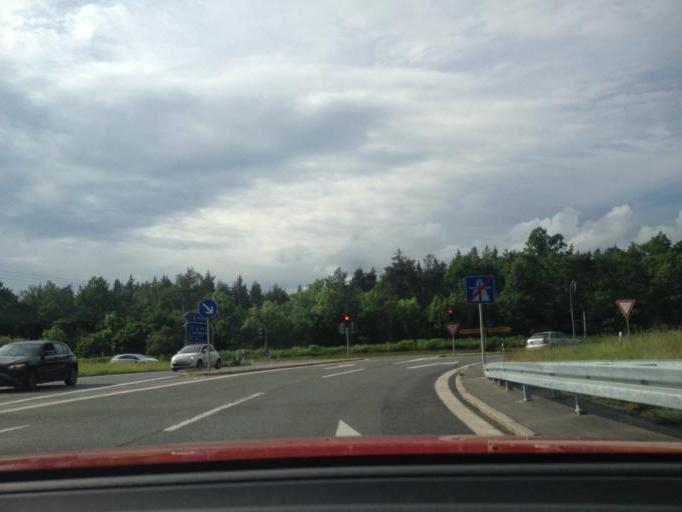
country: DE
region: Bavaria
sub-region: Regierungsbezirk Mittelfranken
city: Schwaig
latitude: 49.4762
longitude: 11.1743
